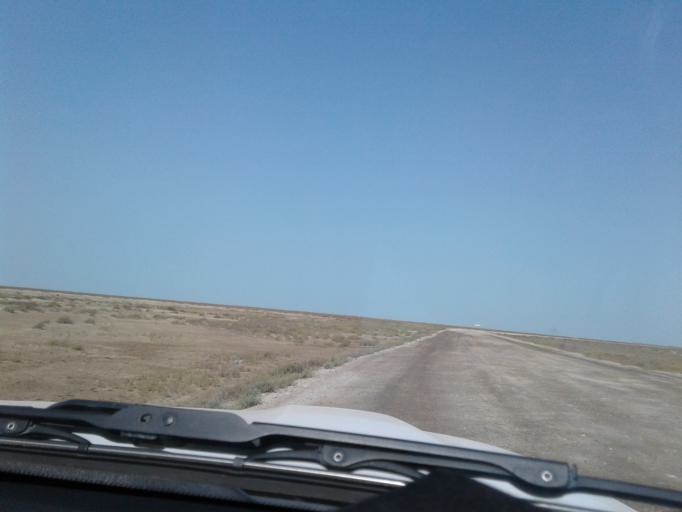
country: IR
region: Golestan
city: Gomishan
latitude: 37.8417
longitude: 53.8891
